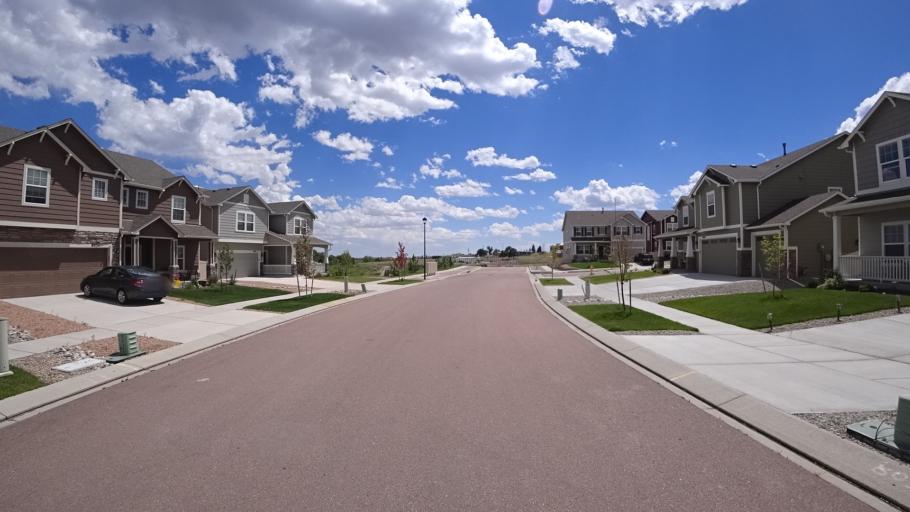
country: US
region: Colorado
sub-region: El Paso County
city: Black Forest
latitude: 38.9495
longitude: -104.7037
